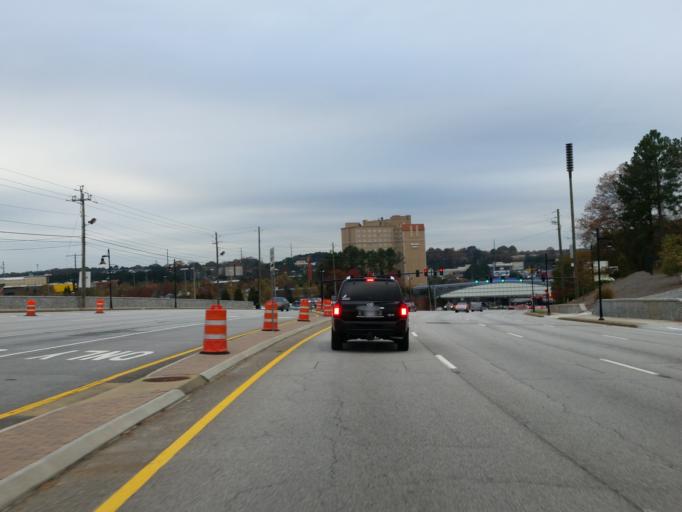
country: US
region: Georgia
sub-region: Cobb County
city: Vinings
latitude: 33.8813
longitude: -84.4650
